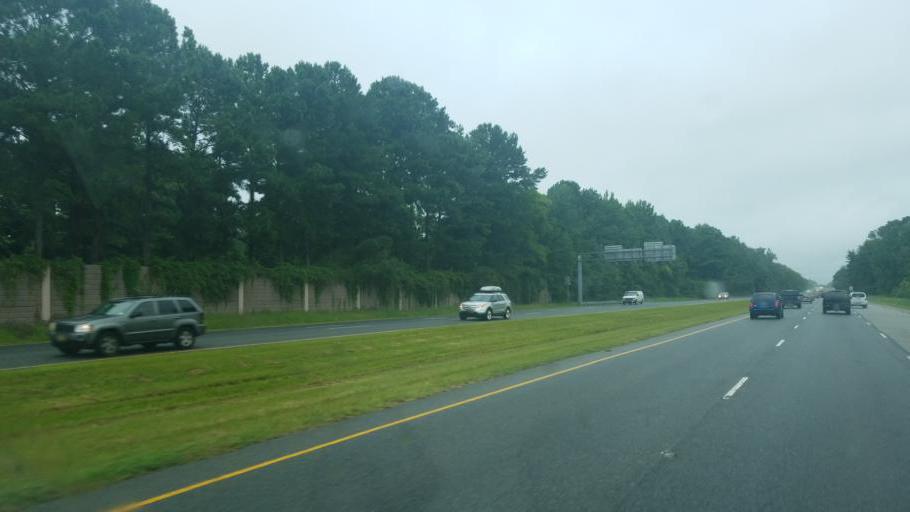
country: US
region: Virginia
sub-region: City of Chesapeake
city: Chesapeake
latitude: 36.6922
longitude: -76.2277
